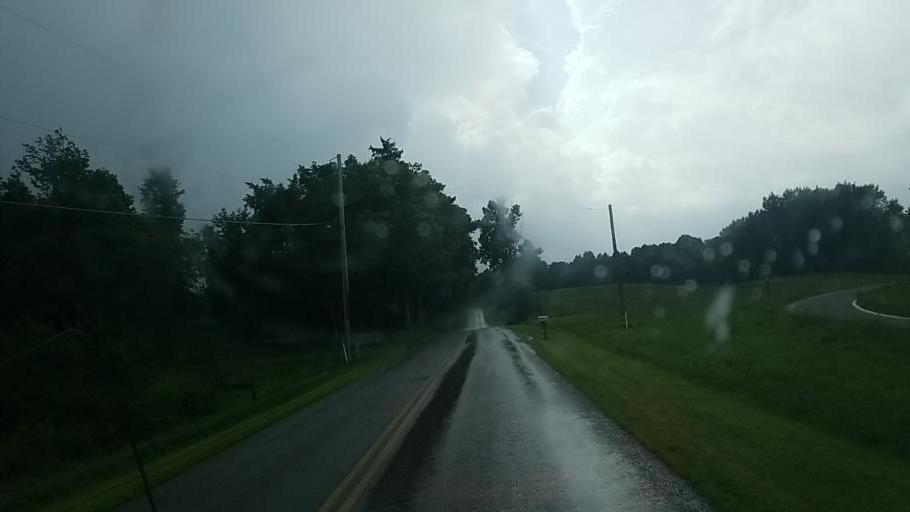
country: US
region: Ohio
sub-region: Champaign County
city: North Lewisburg
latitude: 40.3177
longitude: -83.6042
